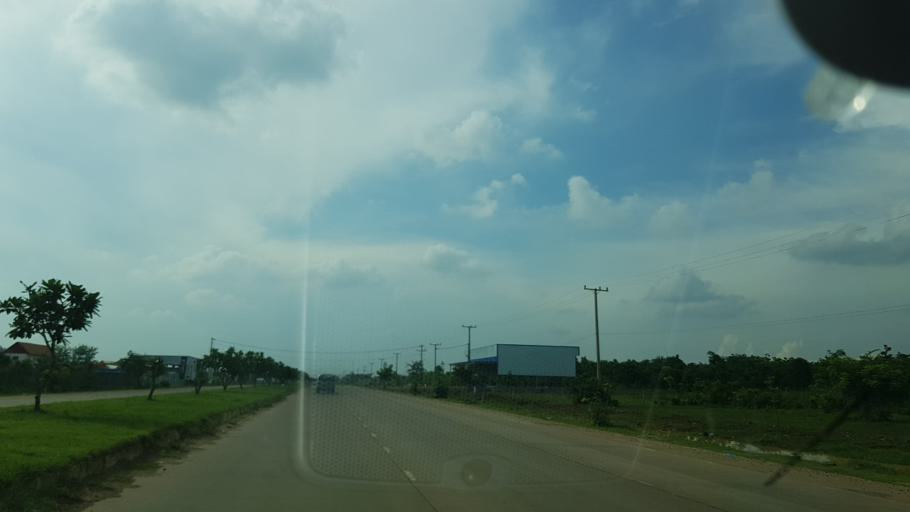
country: LA
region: Vientiane
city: Vientiane
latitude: 17.9951
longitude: 102.7107
